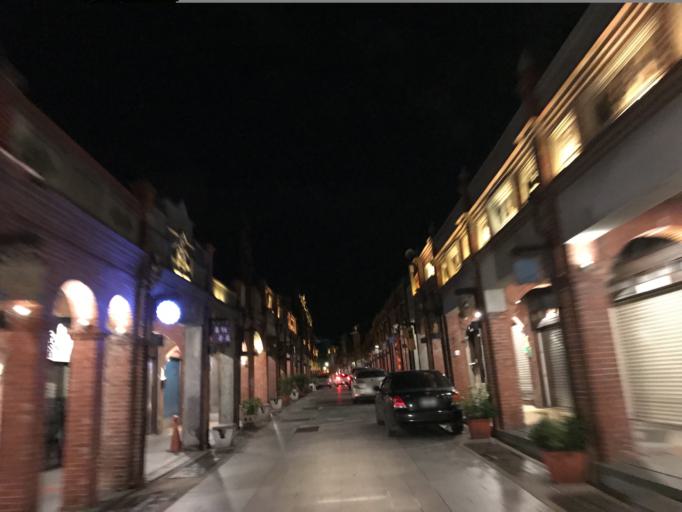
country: TW
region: Taiwan
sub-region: Taoyuan
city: Taoyuan
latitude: 24.9331
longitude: 121.3696
